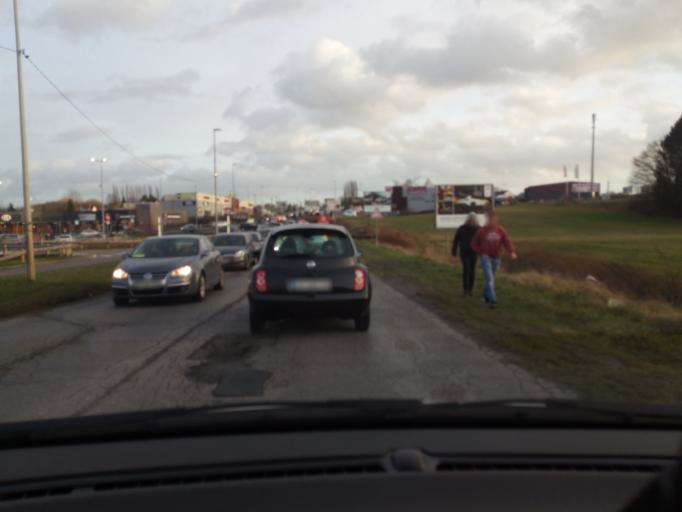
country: FR
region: Nord-Pas-de-Calais
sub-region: Departement du Nord
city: Hautmont
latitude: 50.2530
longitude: 3.9392
